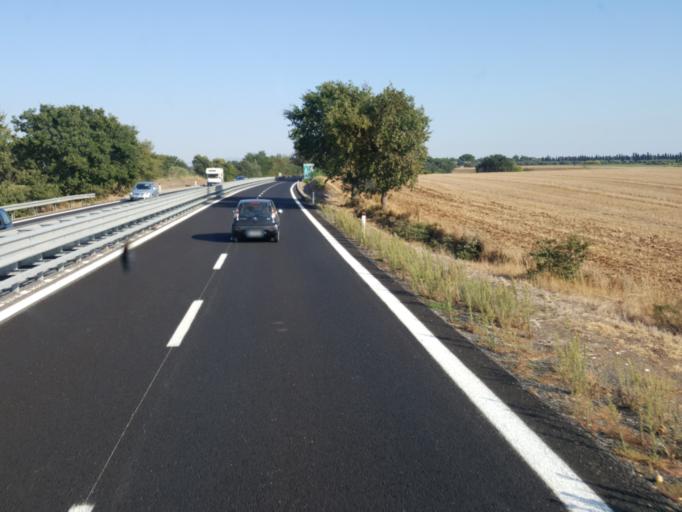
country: IT
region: Latium
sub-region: Provincia di Viterbo
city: Montalto di Castro
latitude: 42.2990
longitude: 11.6728
